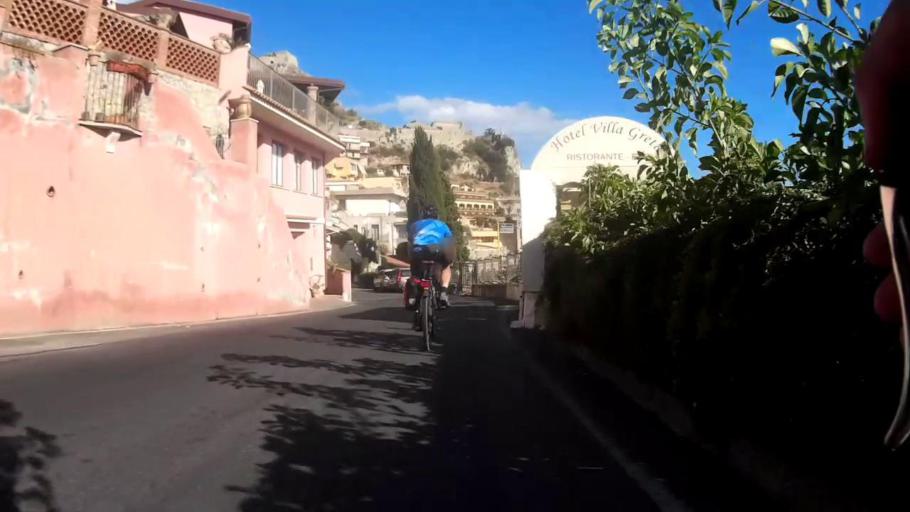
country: IT
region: Sicily
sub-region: Messina
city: Castelmola
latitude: 37.8549
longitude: 15.2812
